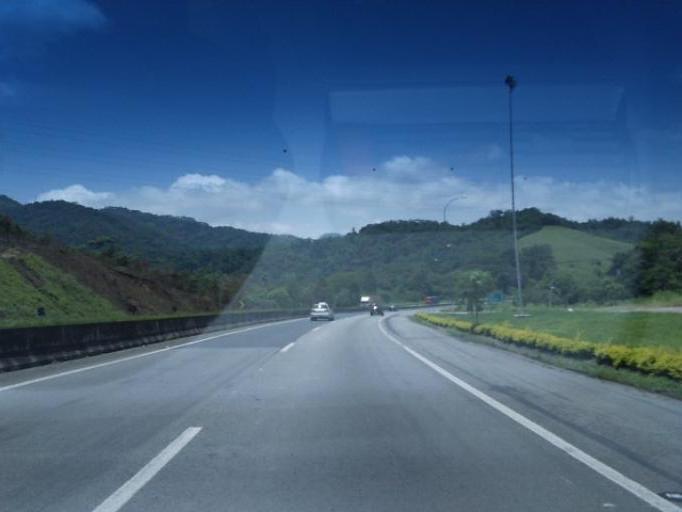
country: BR
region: Sao Paulo
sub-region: Miracatu
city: Miracatu
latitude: -24.2600
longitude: -47.3772
